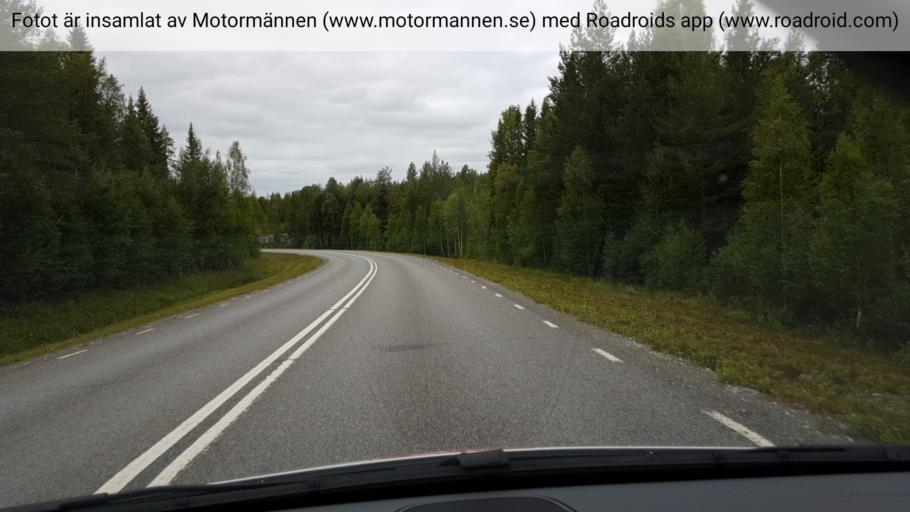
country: SE
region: Jaemtland
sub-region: Stroemsunds Kommun
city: Stroemsund
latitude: 64.3256
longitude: 15.1895
